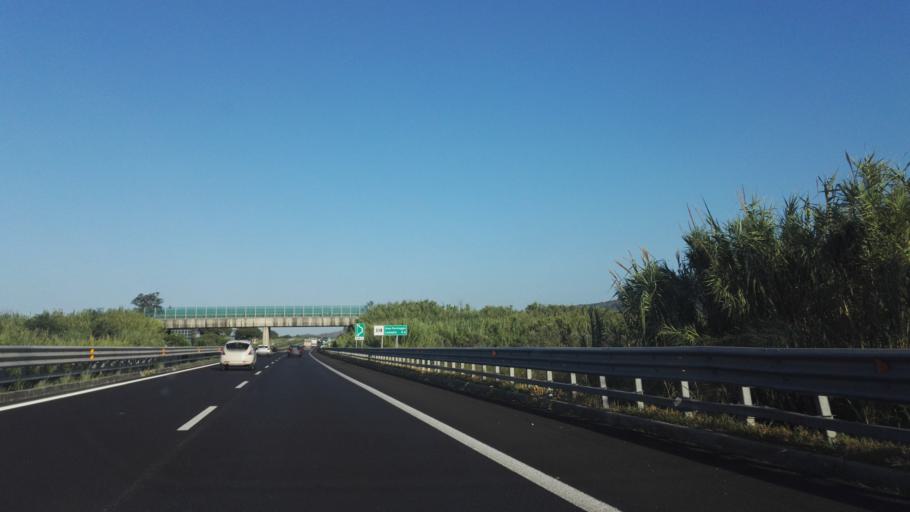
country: IT
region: Calabria
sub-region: Provincia di Catanzaro
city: Santa Eufemia Lamezia
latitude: 38.9316
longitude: 16.2282
